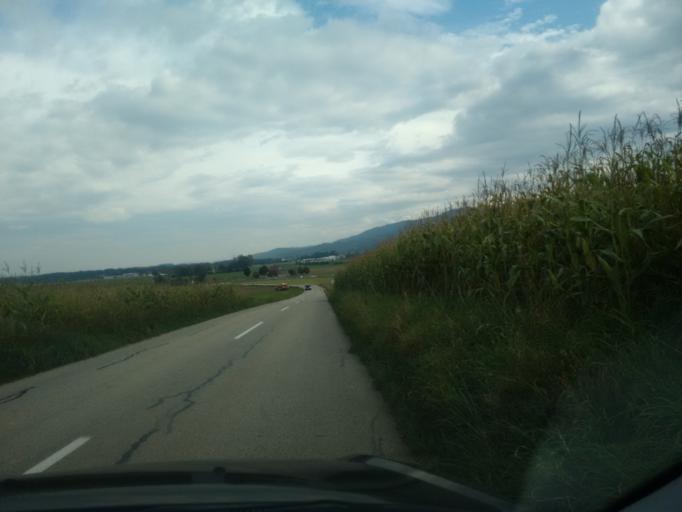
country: AT
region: Upper Austria
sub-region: Politischer Bezirk Vocklabruck
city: Lenzing
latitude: 47.9592
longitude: 13.6371
